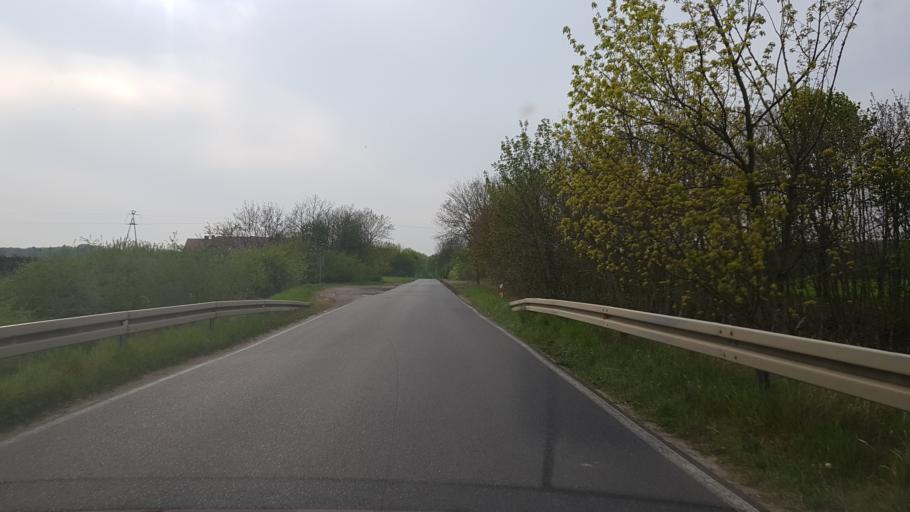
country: PL
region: West Pomeranian Voivodeship
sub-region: Powiat gryfinski
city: Stare Czarnowo
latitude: 53.2829
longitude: 14.7660
